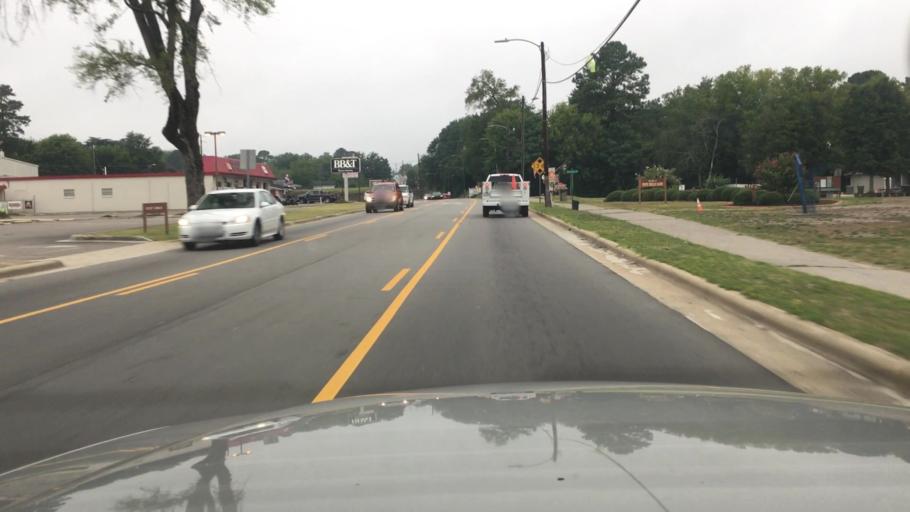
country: US
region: North Carolina
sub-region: Cumberland County
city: Hope Mills
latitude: 34.9731
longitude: -78.9469
